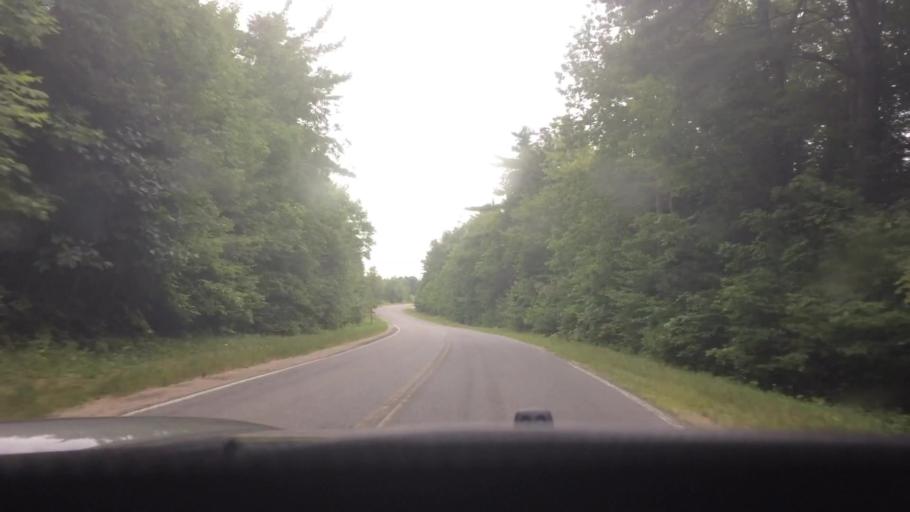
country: US
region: New York
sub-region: St. Lawrence County
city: Hannawa Falls
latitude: 44.5706
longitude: -74.9084
